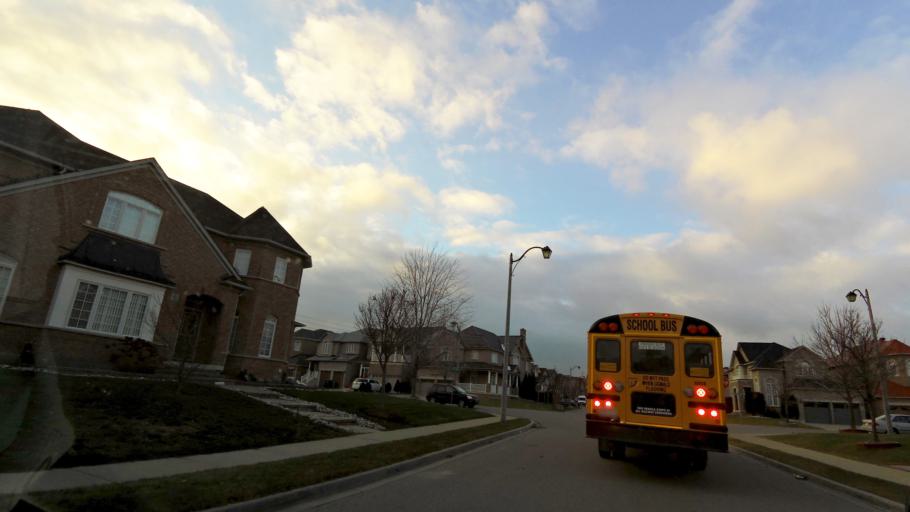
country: CA
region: Ontario
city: Brampton
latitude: 43.7525
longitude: -79.7296
